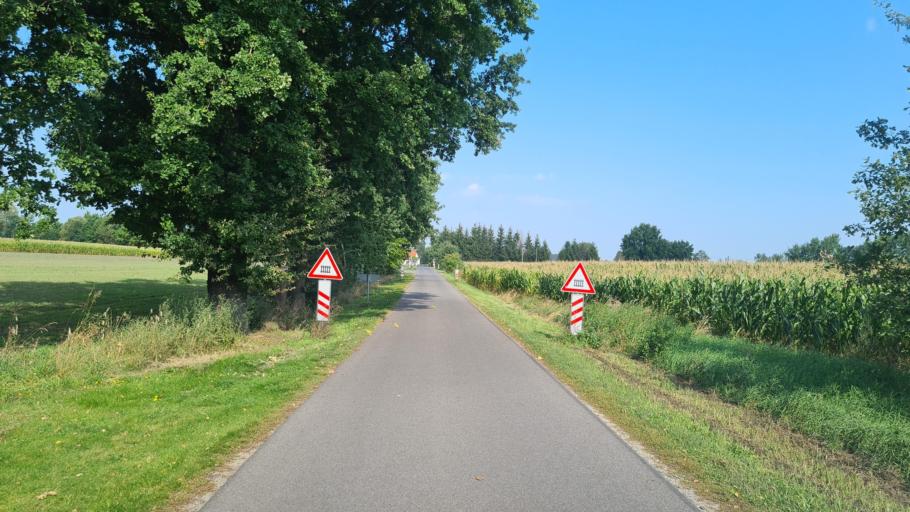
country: DE
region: Brandenburg
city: Kolkwitz
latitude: 51.7421
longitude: 14.2101
